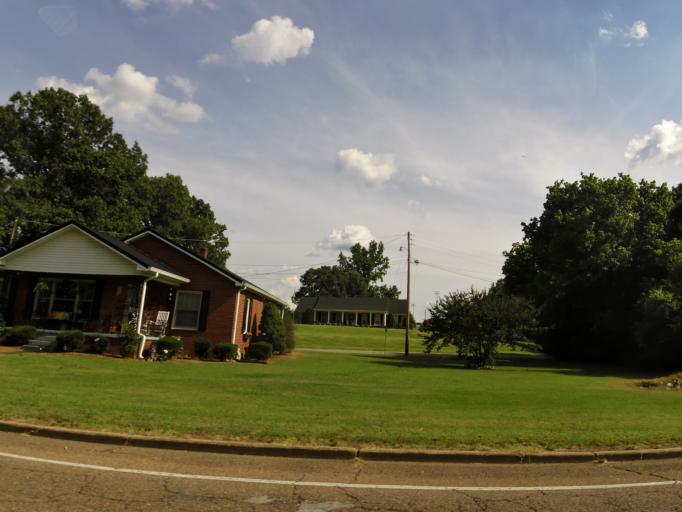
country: US
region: Tennessee
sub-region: Carroll County
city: Bruceton
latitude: 36.0346
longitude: -88.2638
